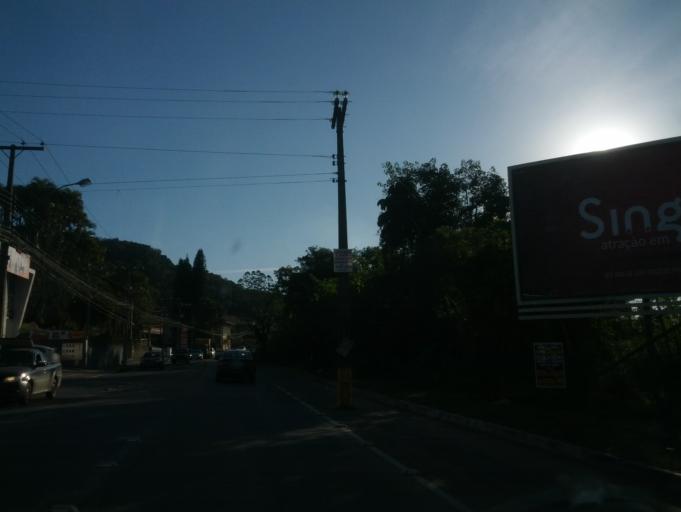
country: BR
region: Santa Catarina
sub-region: Indaial
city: Indaial
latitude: -26.8904
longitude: -49.1966
